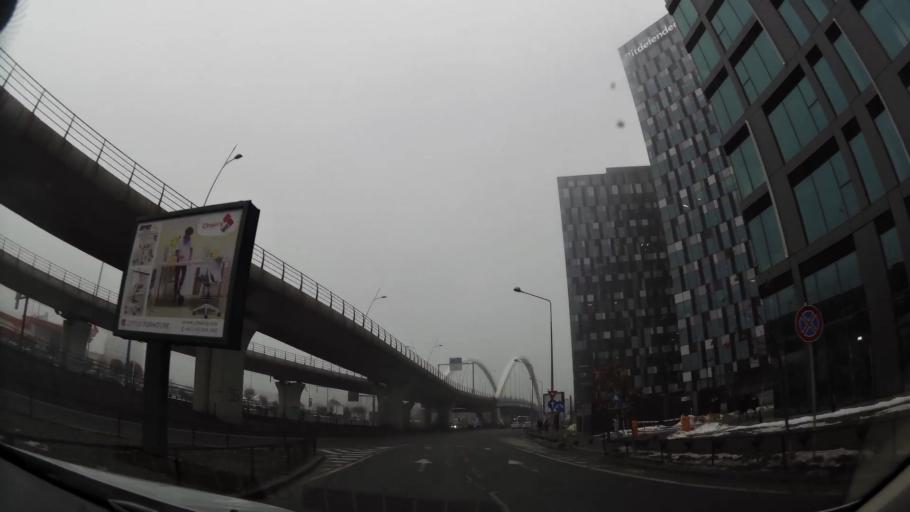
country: RO
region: Bucuresti
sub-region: Municipiul Bucuresti
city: Bucuresti
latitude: 44.4447
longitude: 26.0606
